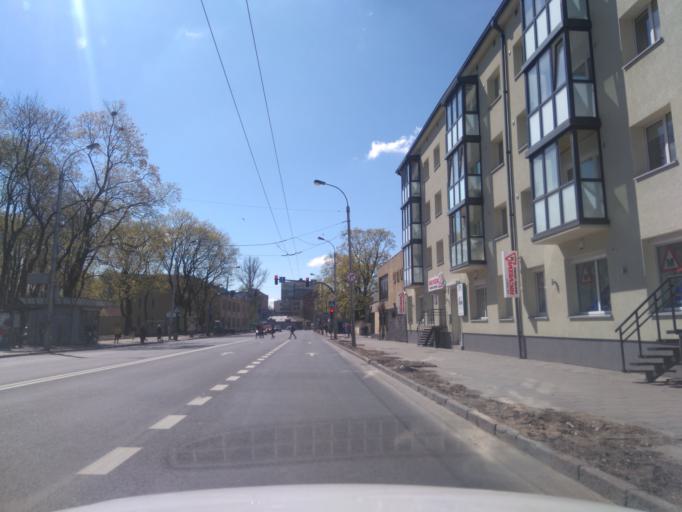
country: LT
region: Kauno apskritis
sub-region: Kaunas
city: Kaunas
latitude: 54.8928
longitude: 23.9246
